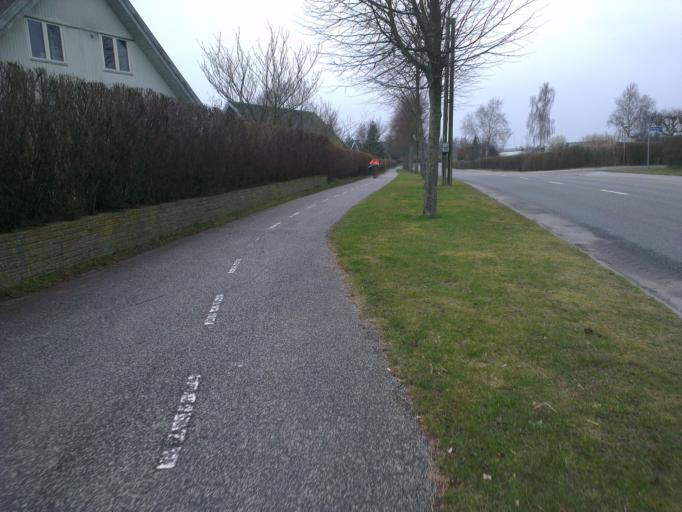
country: DK
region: Capital Region
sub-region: Frederikssund Kommune
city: Slangerup
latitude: 55.8389
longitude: 12.1777
